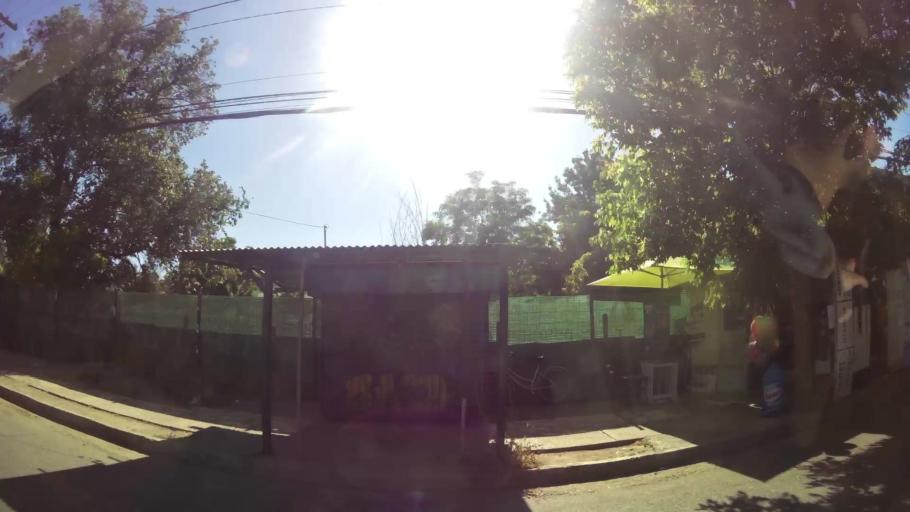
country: CL
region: Santiago Metropolitan
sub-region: Provincia de Chacabuco
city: Lampa
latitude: -33.4034
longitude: -71.1288
